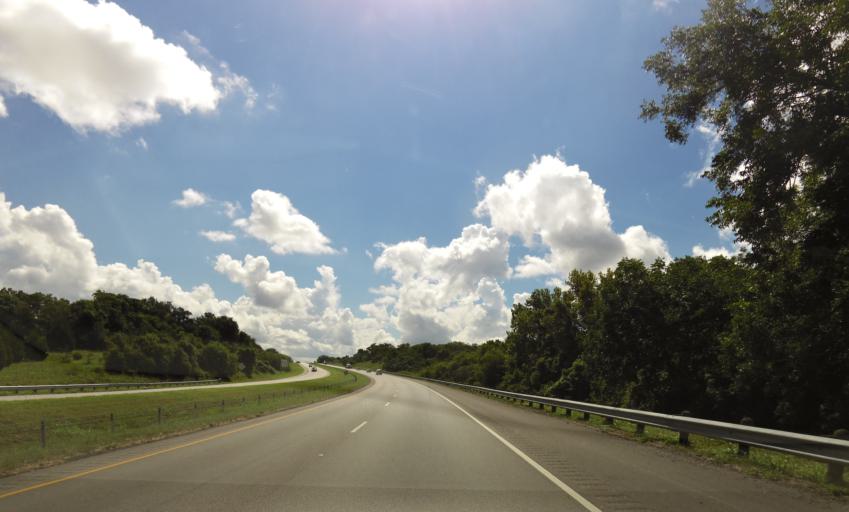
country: US
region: Texas
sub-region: Colorado County
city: Weimar
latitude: 29.6876
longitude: -96.8331
